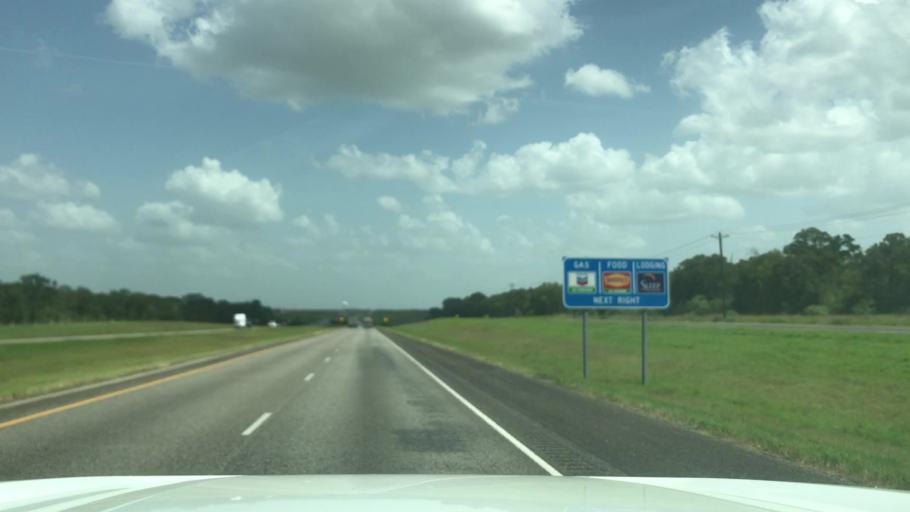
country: US
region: Texas
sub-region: Brazos County
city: Bryan
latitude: 30.7360
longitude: -96.4373
